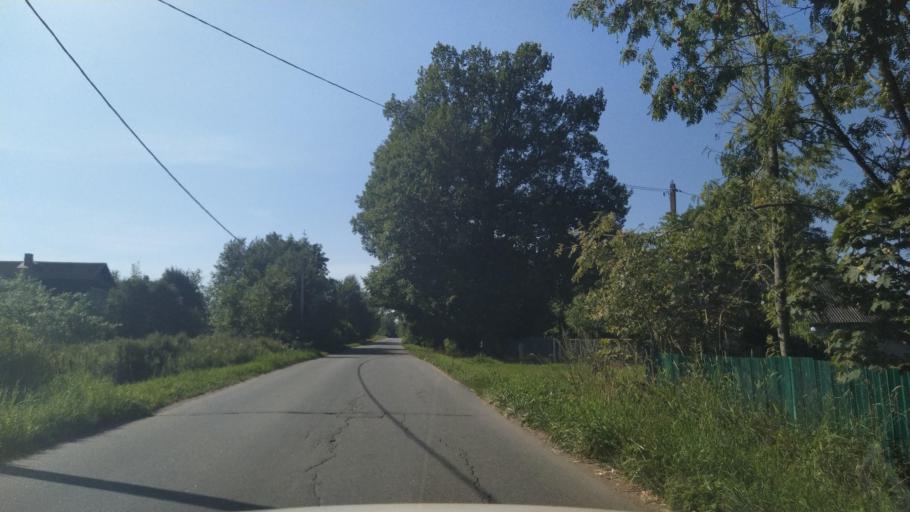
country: RU
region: Leningrad
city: Siverskiy
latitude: 59.2726
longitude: 30.0460
